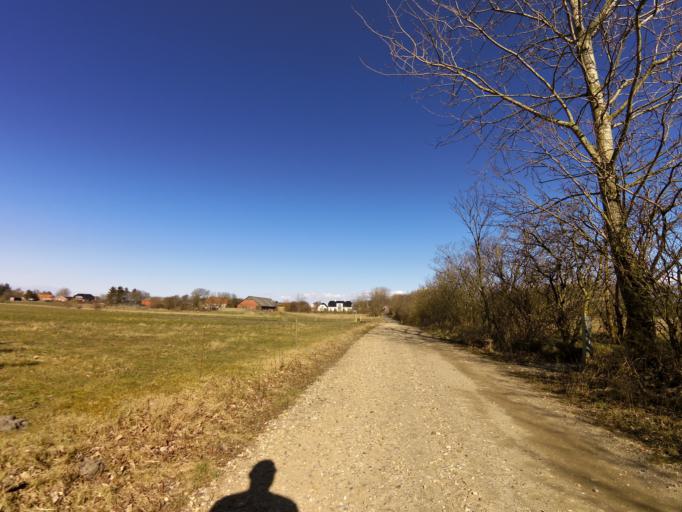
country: DK
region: South Denmark
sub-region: Varde Kommune
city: Varde
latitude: 55.5894
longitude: 8.4099
